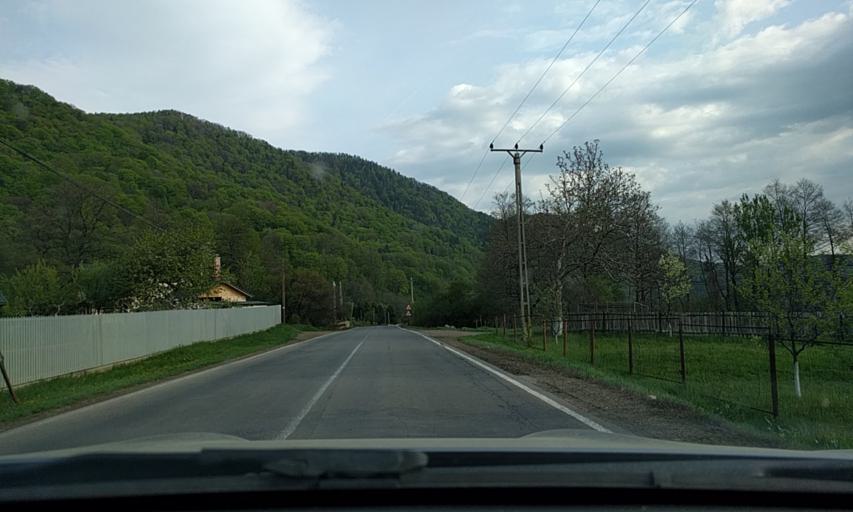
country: RO
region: Bacau
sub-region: Oras Slanic-Moldova
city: Slanic-Moldova
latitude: 46.1495
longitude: 26.4596
